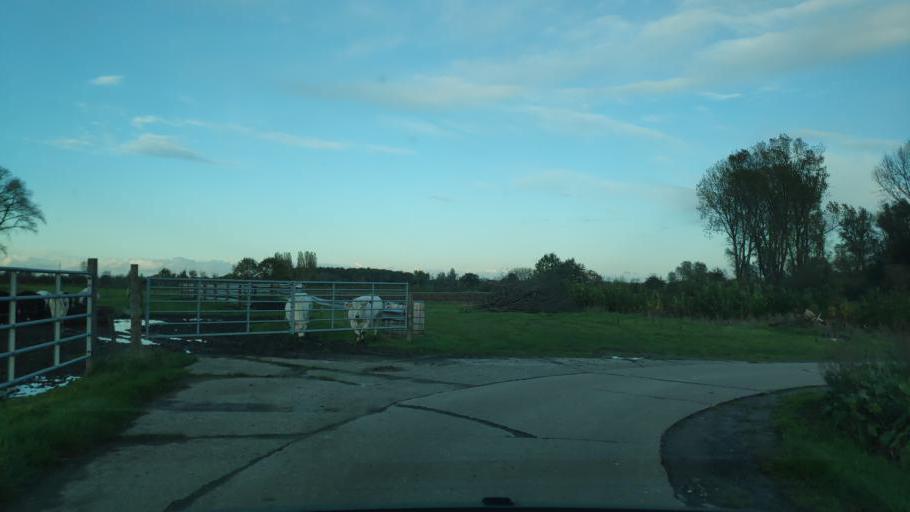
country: BE
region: Flanders
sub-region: Provincie Oost-Vlaanderen
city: Aalter
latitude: 51.1010
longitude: 3.4862
